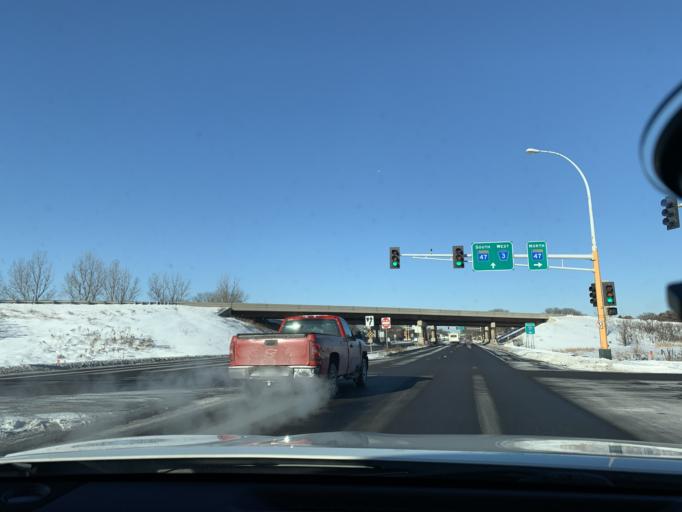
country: US
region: Minnesota
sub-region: Anoka County
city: Coon Rapids
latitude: 45.1351
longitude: -93.2691
